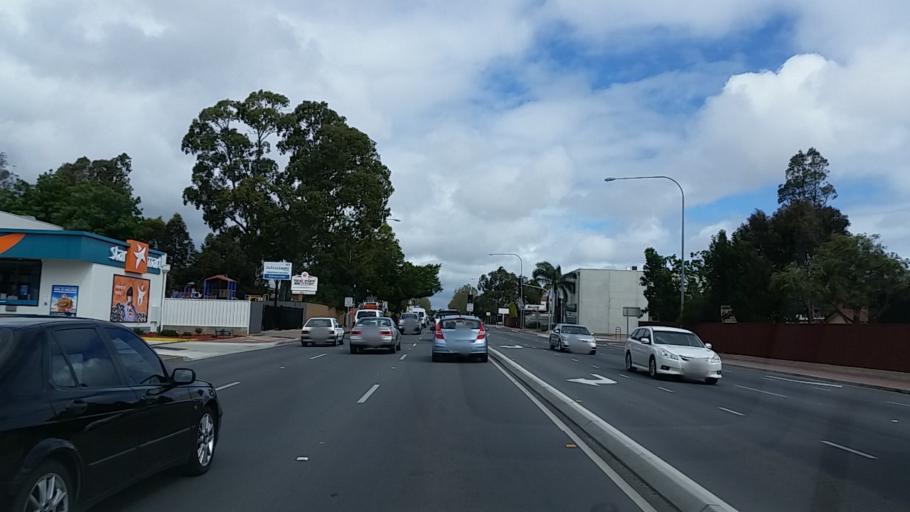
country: AU
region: South Australia
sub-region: Unley
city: Forestville
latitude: -34.9423
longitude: 138.5711
